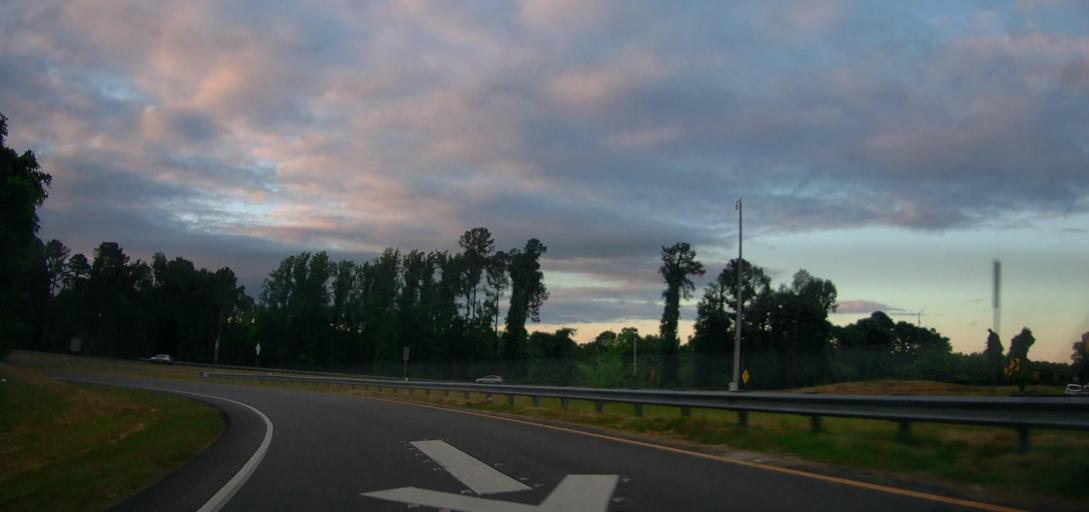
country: US
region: Georgia
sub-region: Clarke County
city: Country Club Estates
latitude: 33.9704
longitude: -83.4070
